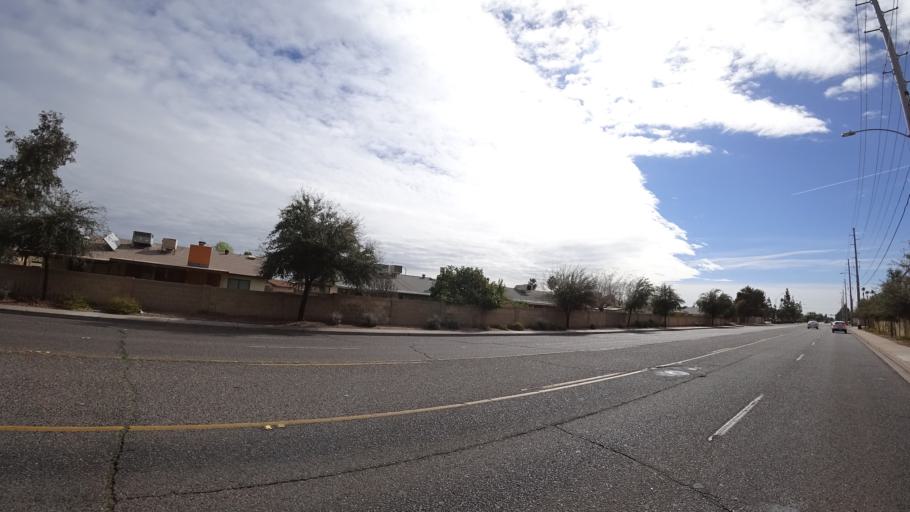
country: US
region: Arizona
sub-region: Maricopa County
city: Peoria
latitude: 33.6284
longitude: -112.1858
